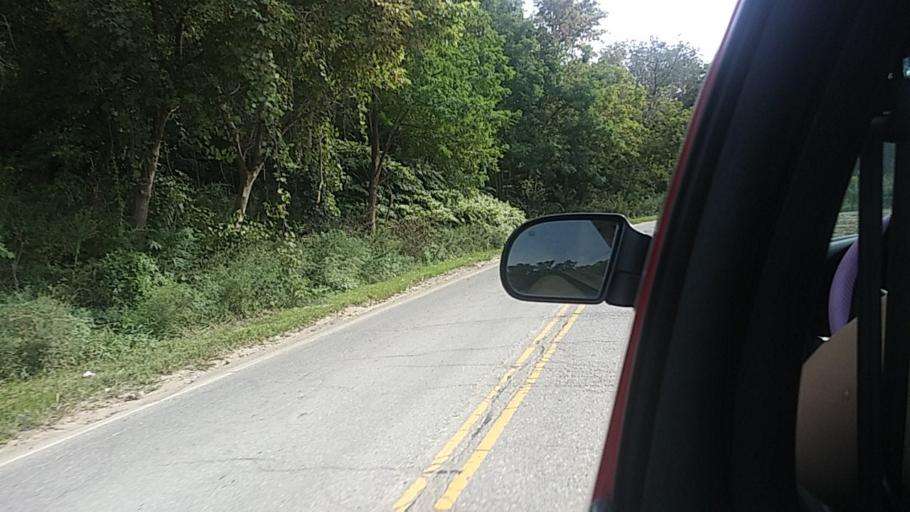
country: US
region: Ohio
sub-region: Summit County
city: Akron
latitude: 41.0951
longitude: -81.4852
